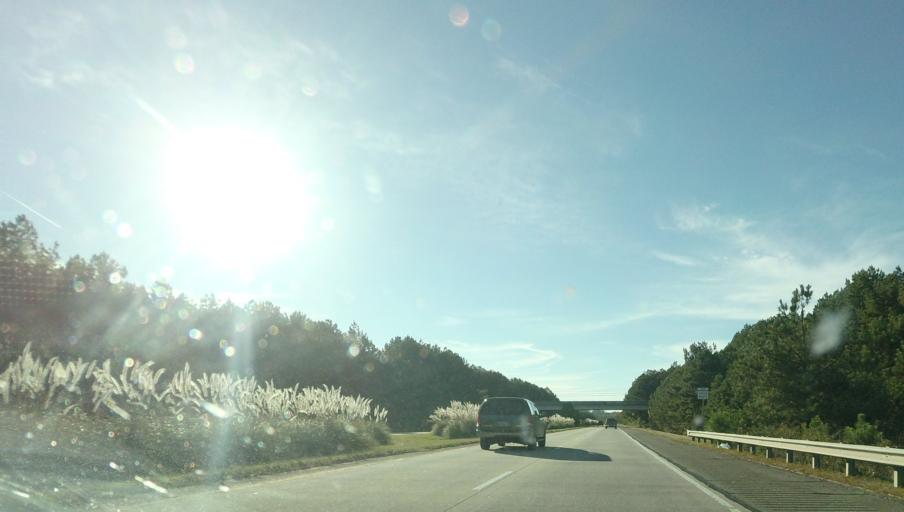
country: US
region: Georgia
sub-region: Muscogee County
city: Columbus
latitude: 32.5544
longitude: -84.9040
